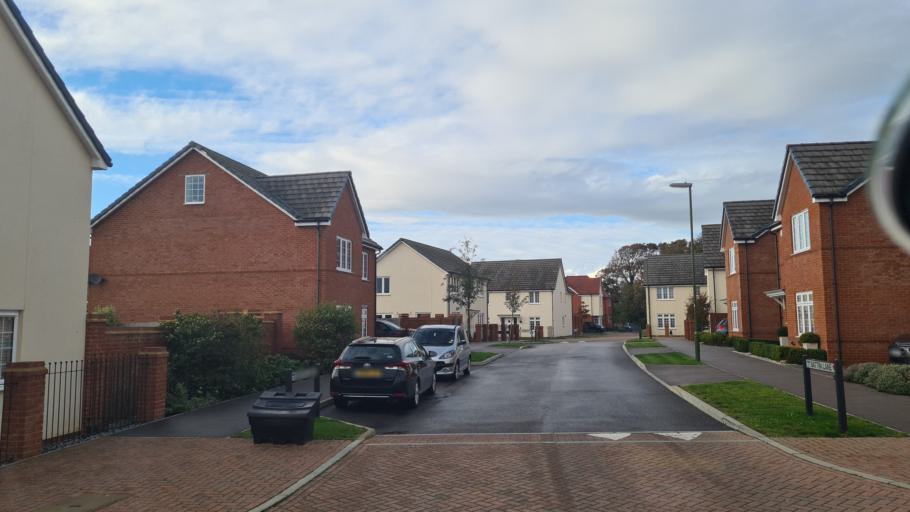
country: GB
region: England
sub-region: West Sussex
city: Littlehampton
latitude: 50.8247
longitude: -0.5593
